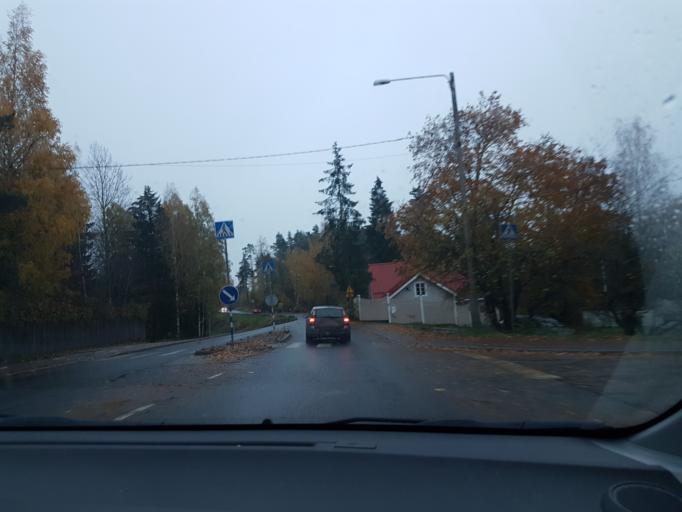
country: FI
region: Uusimaa
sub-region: Helsinki
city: Tuusula
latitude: 60.4049
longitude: 25.0157
